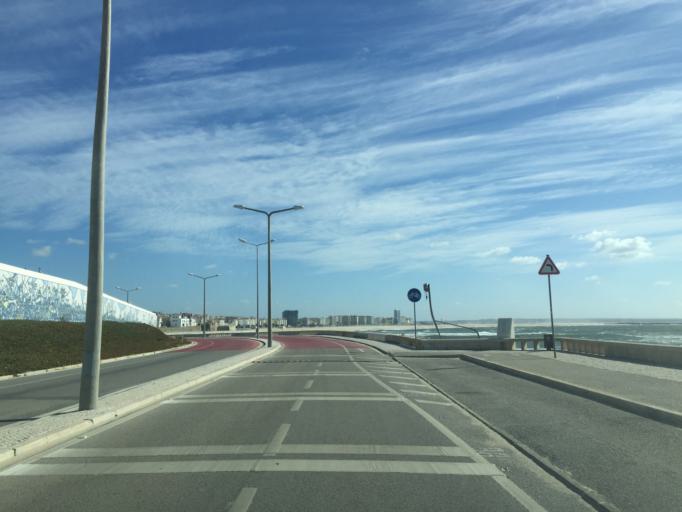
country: PT
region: Coimbra
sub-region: Figueira da Foz
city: Buarcos
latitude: 40.1670
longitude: -8.8851
